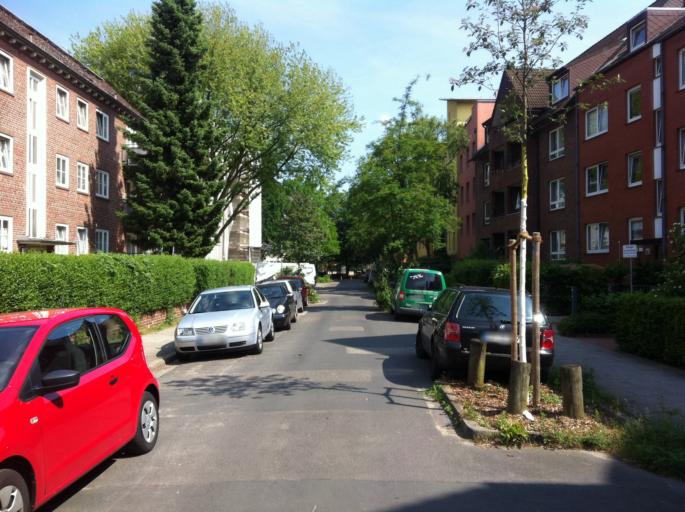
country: DE
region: Hamburg
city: St. Pauli
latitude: 53.5521
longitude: 9.9510
